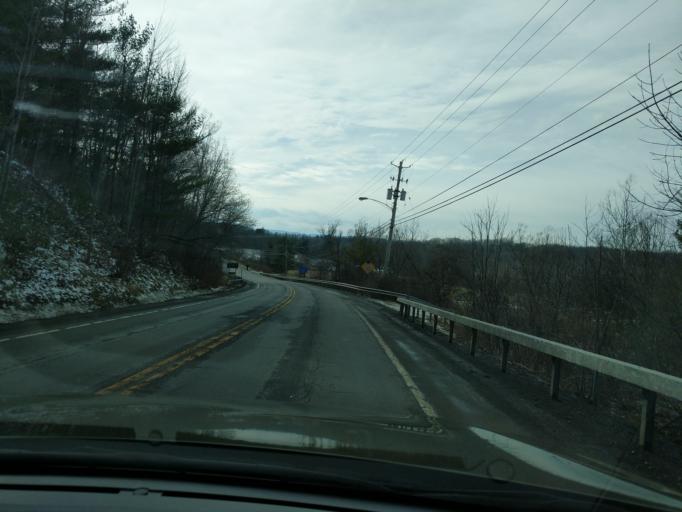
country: US
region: New York
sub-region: Tompkins County
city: Northeast Ithaca
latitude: 42.4585
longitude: -76.4326
